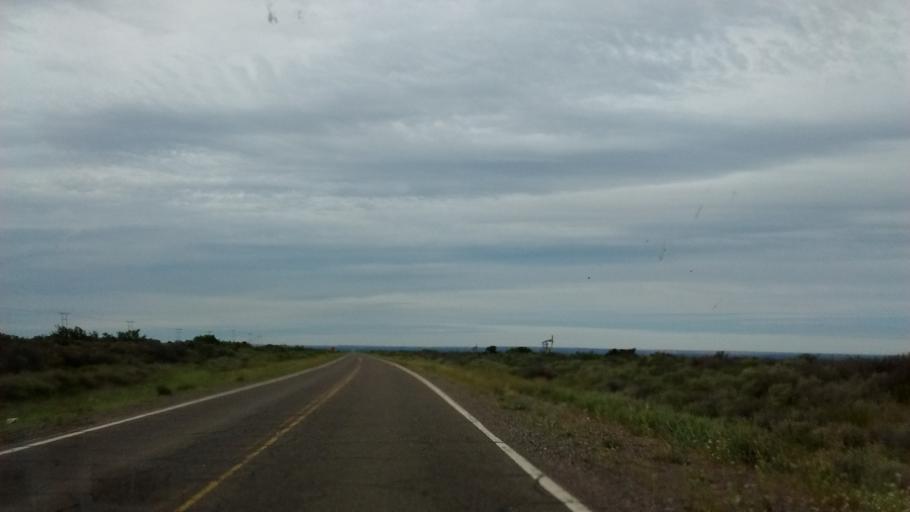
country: AR
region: Rio Negro
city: Catriel
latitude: -37.9826
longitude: -67.9085
